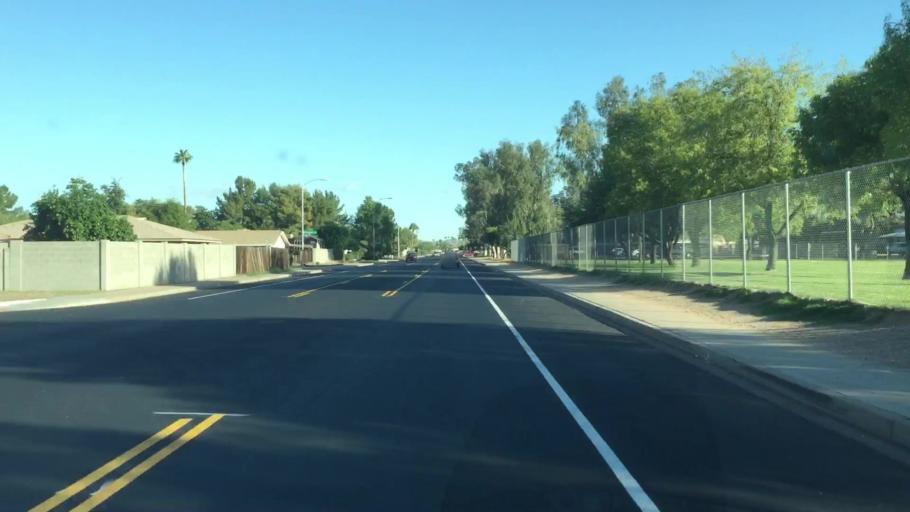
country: US
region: Arizona
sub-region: Maricopa County
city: Gilbert
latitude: 33.4015
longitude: -111.7625
